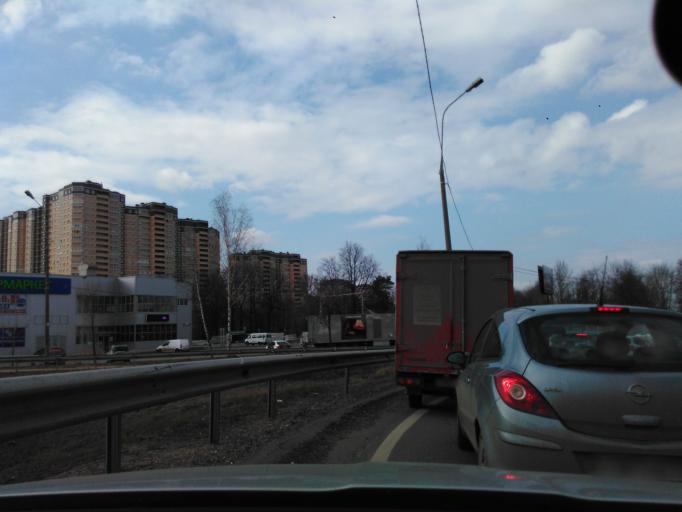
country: RU
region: Moskovskaya
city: Dolgoprudnyy
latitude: 55.9674
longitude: 37.5325
